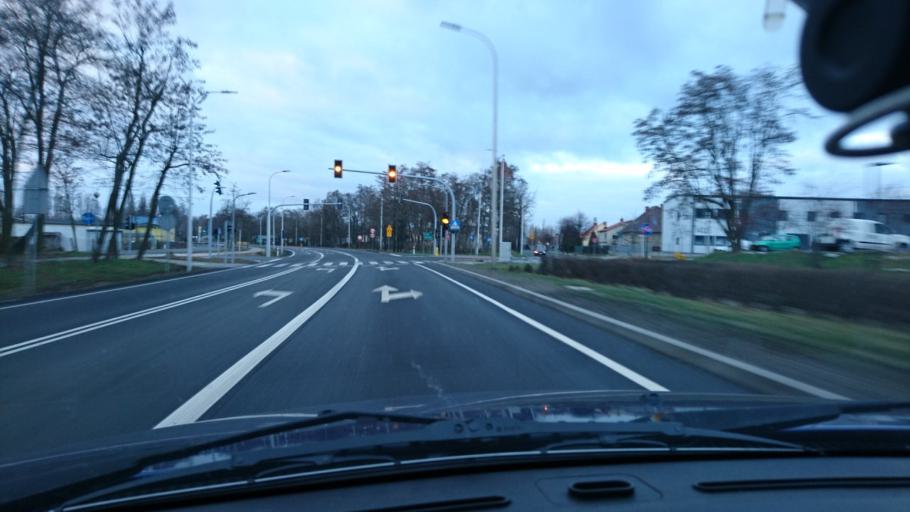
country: PL
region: Greater Poland Voivodeship
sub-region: Powiat ostrzeszowski
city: Ostrzeszow
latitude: 51.4174
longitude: 17.9317
